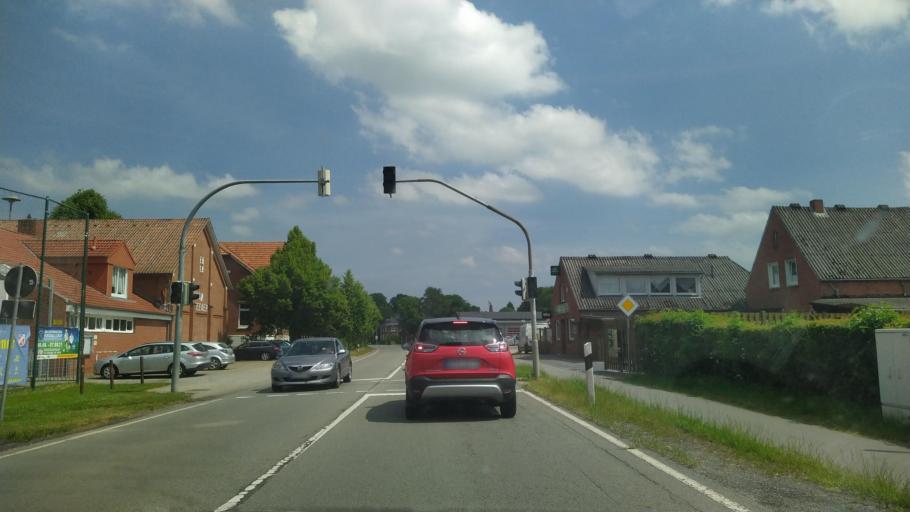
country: DE
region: Lower Saxony
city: Weener
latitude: 53.1673
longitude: 7.3426
